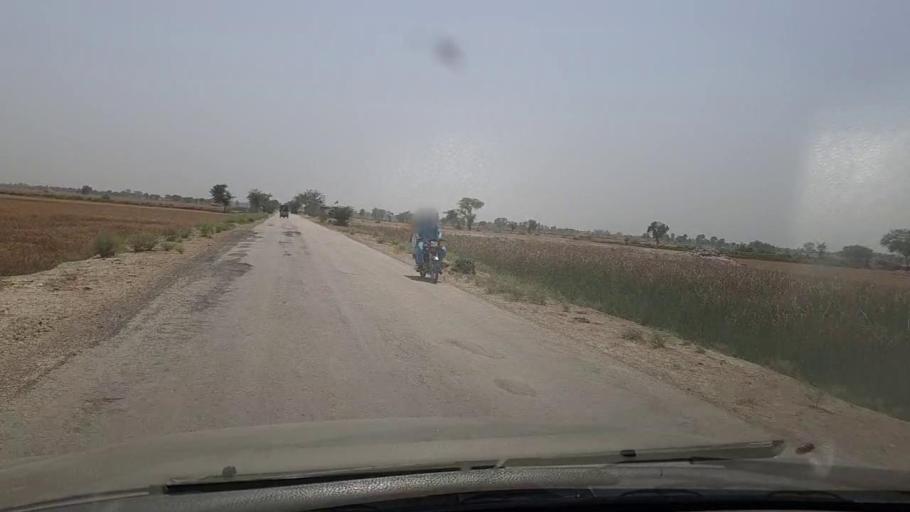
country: PK
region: Sindh
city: Miro Khan
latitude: 27.6959
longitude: 68.0589
